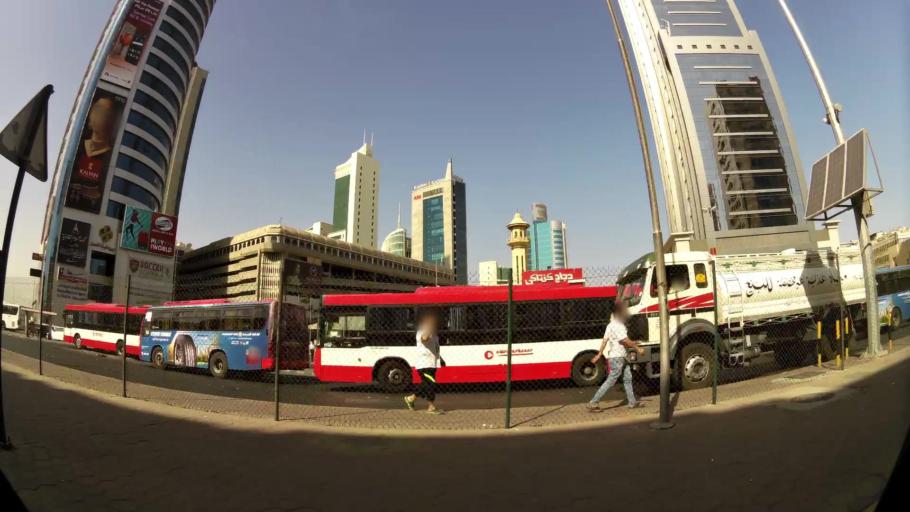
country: KW
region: Al Asimah
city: Ash Shamiyah
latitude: 29.3624
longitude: 47.9647
